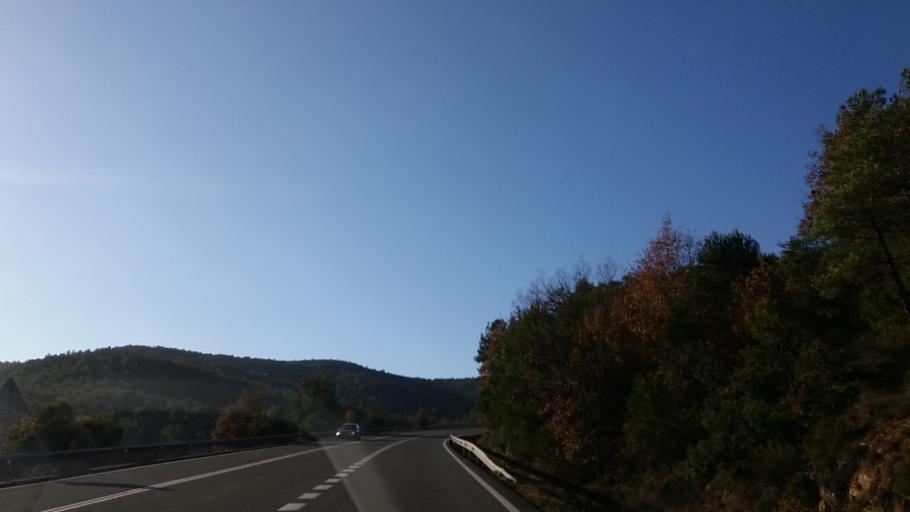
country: ES
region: Catalonia
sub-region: Provincia de Lleida
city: Tiurana
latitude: 41.9599
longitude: 1.2908
